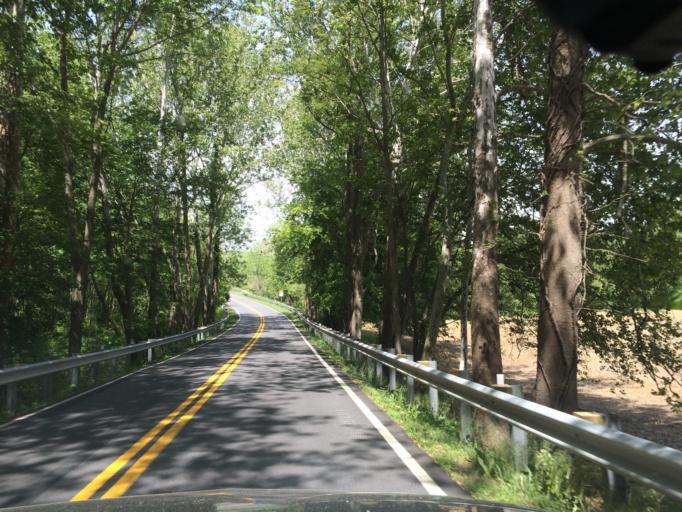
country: US
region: Maryland
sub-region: Carroll County
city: Westminster
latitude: 39.5177
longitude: -76.9507
